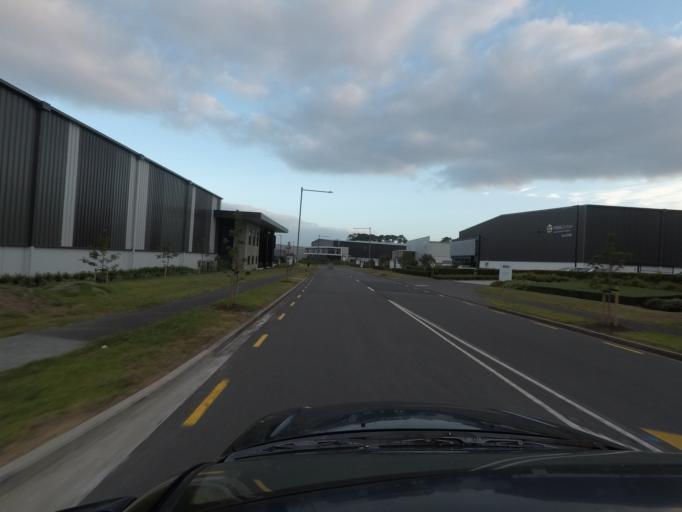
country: NZ
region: Auckland
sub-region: Auckland
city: Tamaki
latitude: -36.9350
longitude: 174.8763
